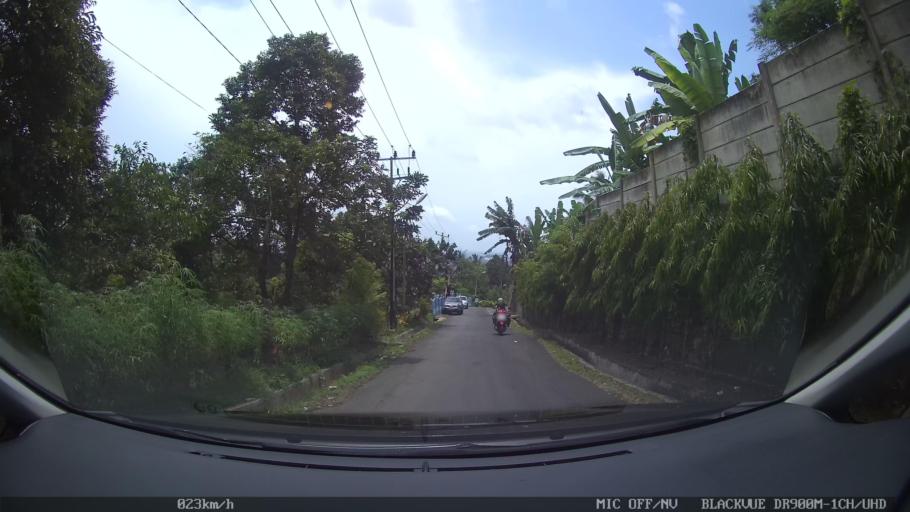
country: ID
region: Lampung
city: Bandarlampung
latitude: -5.4216
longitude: 105.2312
